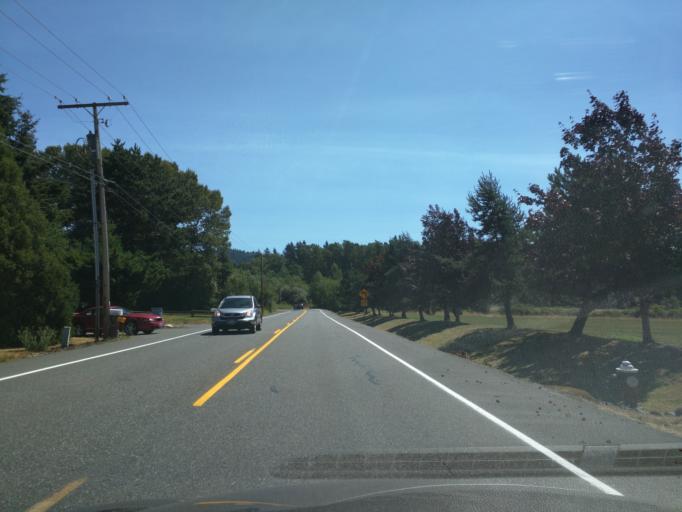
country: US
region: Washington
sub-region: Whatcom County
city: Geneva
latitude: 48.7894
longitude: -122.4360
